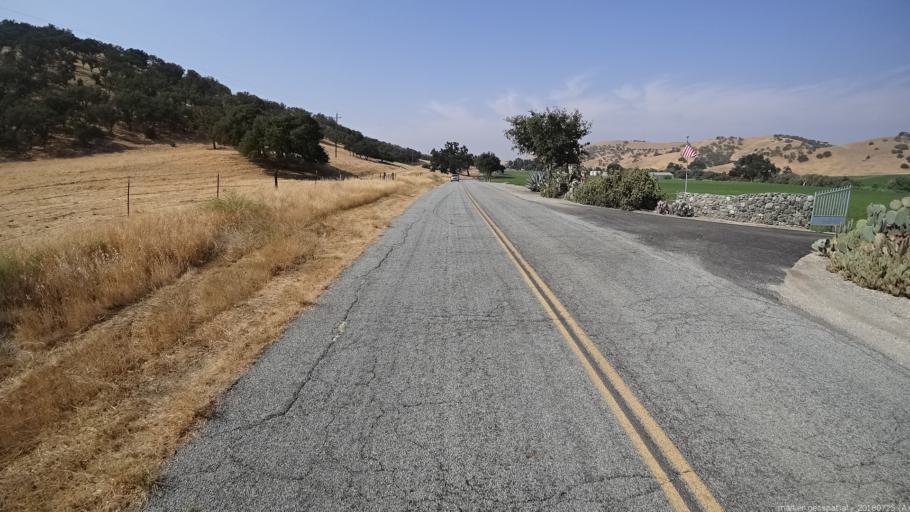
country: US
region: California
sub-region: San Luis Obispo County
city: San Miguel
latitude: 35.8126
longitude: -120.6668
